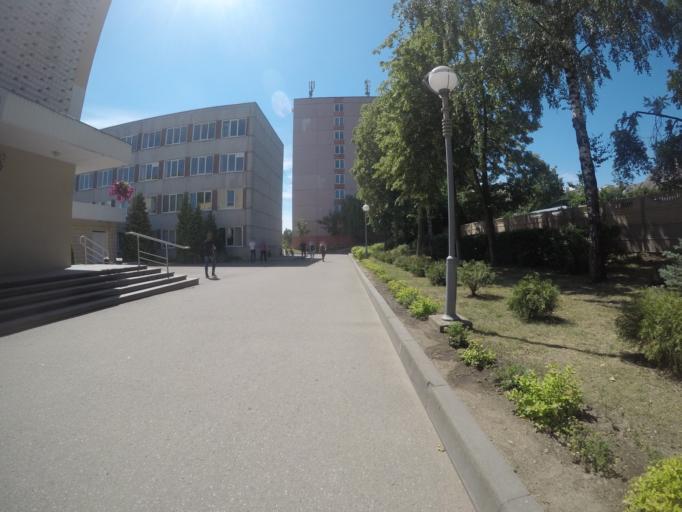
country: BY
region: Grodnenskaya
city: Hrodna
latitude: 53.6982
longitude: 23.8410
